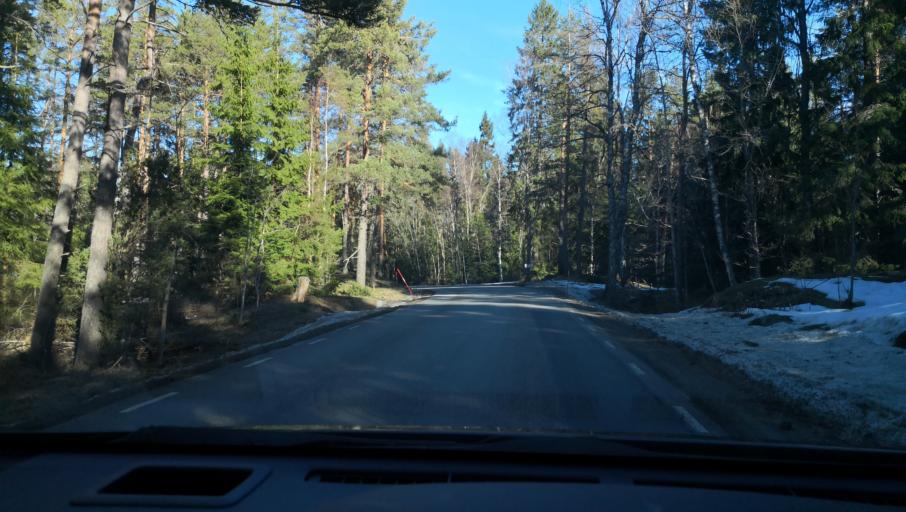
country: SE
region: Uppsala
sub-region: Osthammars Kommun
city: Osterbybruk
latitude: 60.2218
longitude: 17.9177
